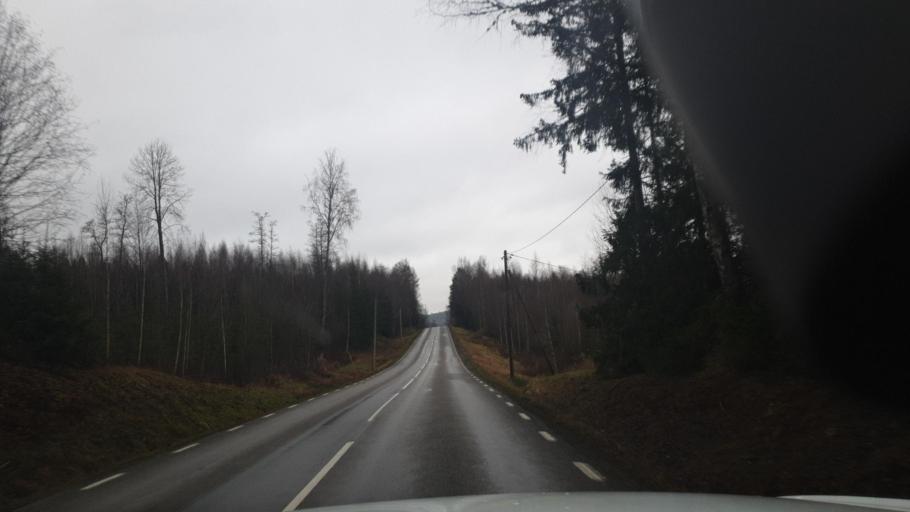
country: SE
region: Vaermland
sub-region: Eda Kommun
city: Amotfors
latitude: 59.6629
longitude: 12.4268
